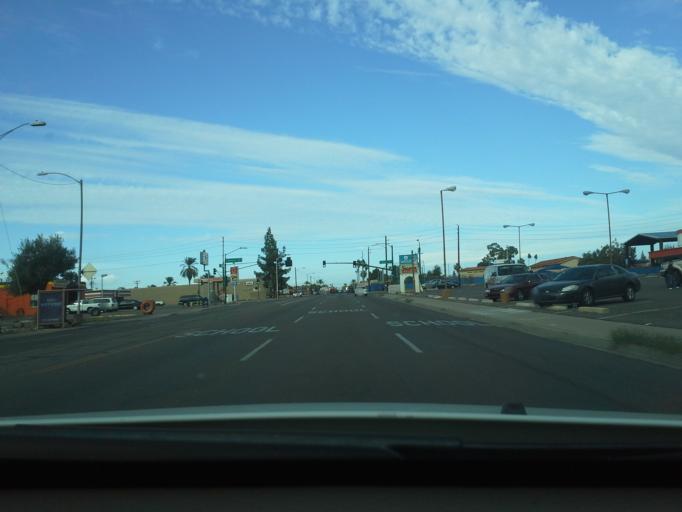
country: US
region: Arizona
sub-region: Maricopa County
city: Phoenix
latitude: 33.4867
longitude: -112.0999
